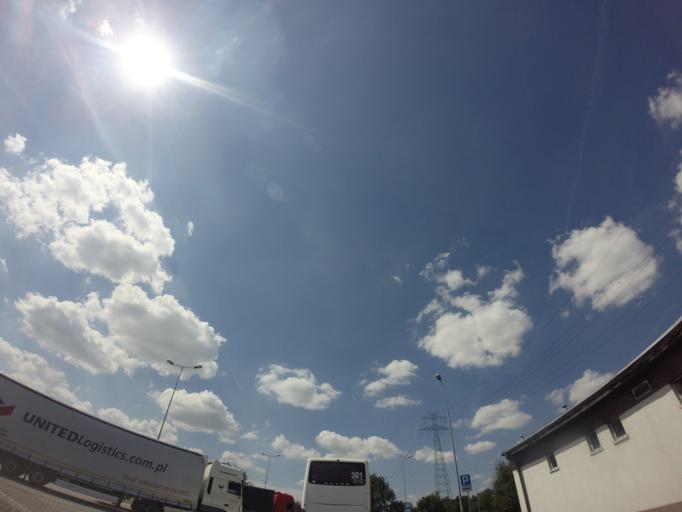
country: PL
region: Lower Silesian Voivodeship
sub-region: Powiat strzelinski
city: Wiazow
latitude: 50.8464
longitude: 17.2530
